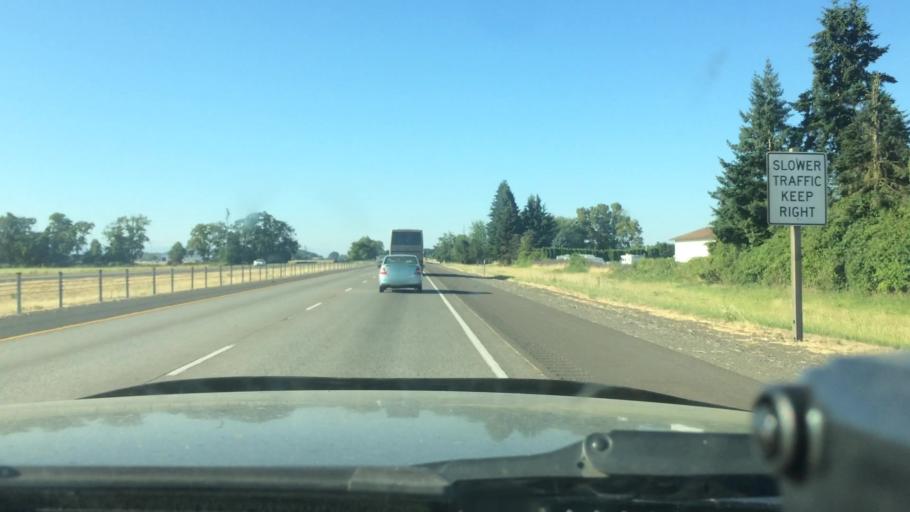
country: US
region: Oregon
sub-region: Linn County
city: Albany
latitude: 44.6083
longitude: -123.0634
